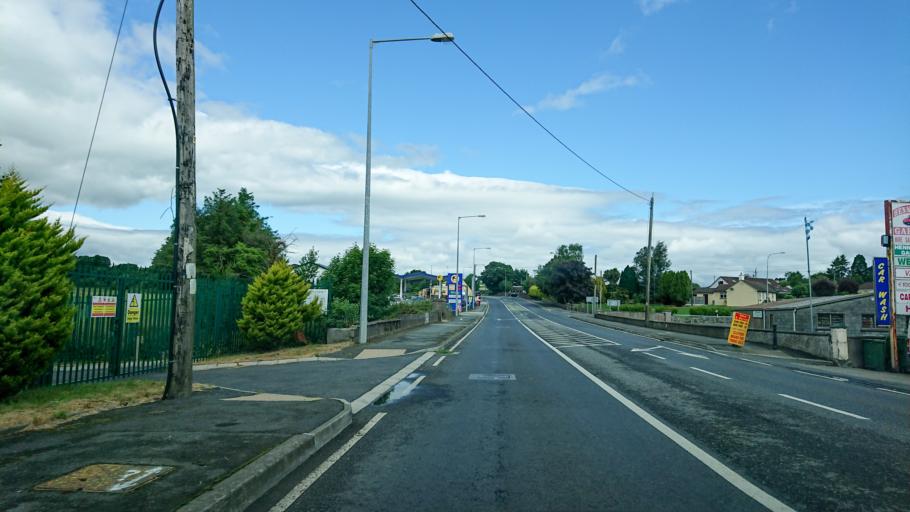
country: IE
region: Leinster
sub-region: Kilkenny
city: Mooncoin
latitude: 52.2334
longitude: -7.2430
